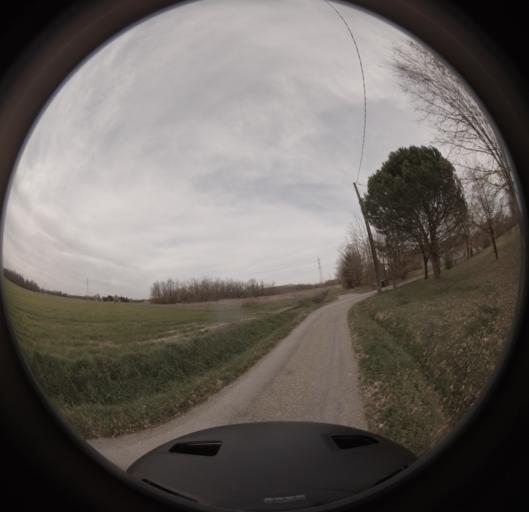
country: FR
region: Midi-Pyrenees
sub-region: Departement du Tarn-et-Garonne
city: Montbeton
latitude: 43.9929
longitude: 1.2753
